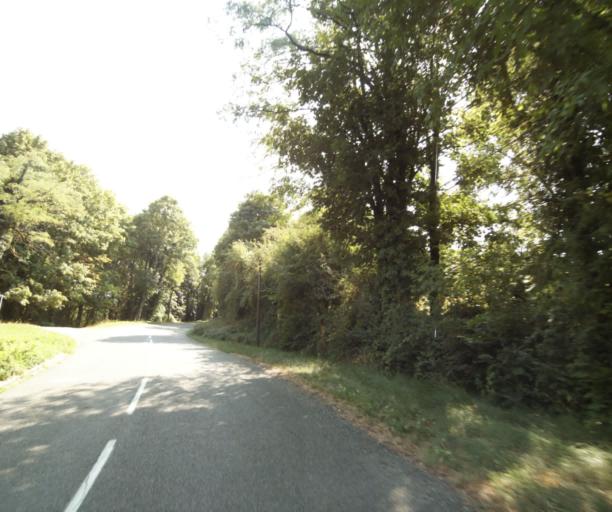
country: FR
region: Bourgogne
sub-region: Departement de Saone-et-Loire
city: Tournus
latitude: 46.5594
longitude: 4.8776
